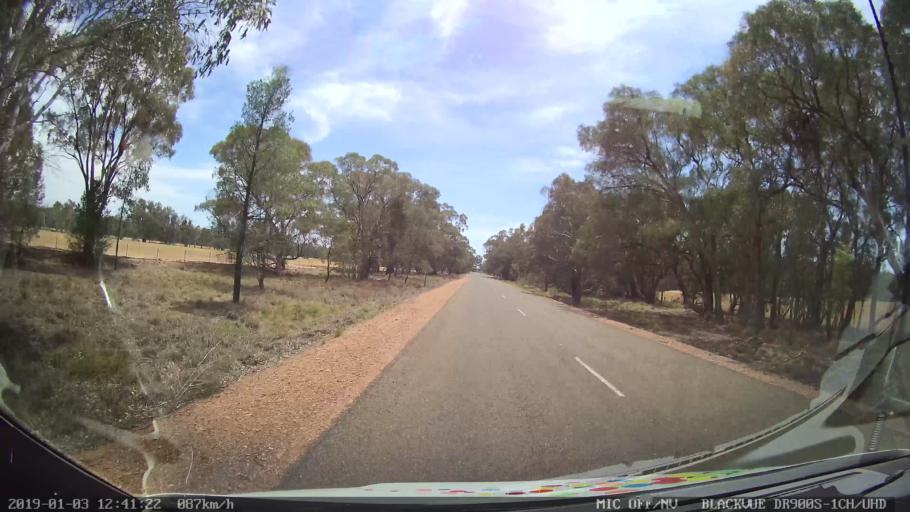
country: AU
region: New South Wales
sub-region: Weddin
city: Grenfell
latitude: -33.8006
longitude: 148.2149
